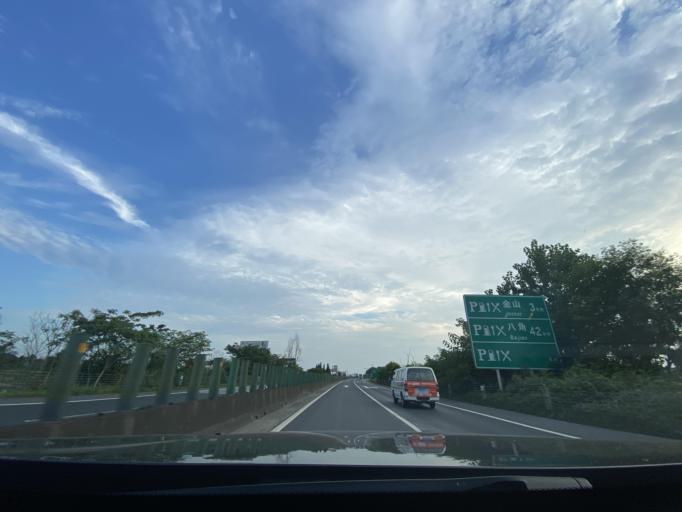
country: CN
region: Sichuan
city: Luojiang
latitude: 31.3816
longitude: 104.5514
